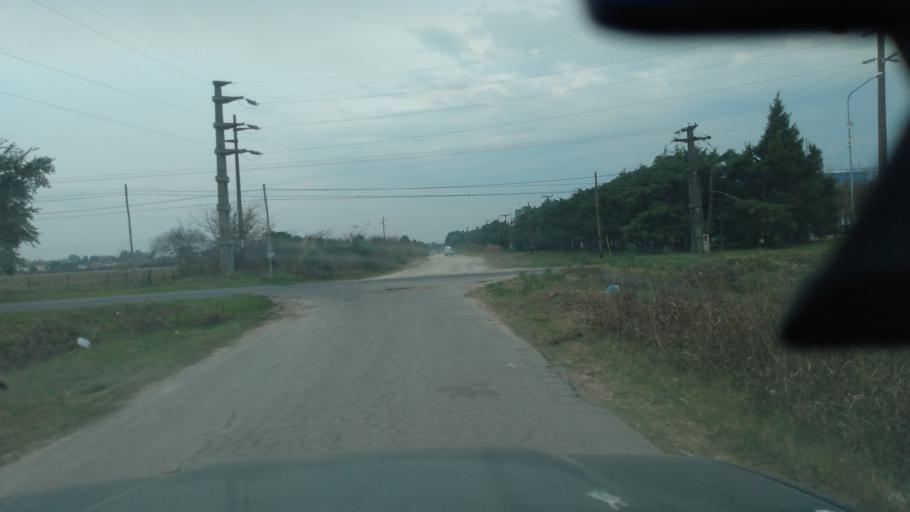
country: AR
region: Buenos Aires
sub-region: Partido de Lujan
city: Lujan
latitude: -34.5641
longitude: -59.1419
